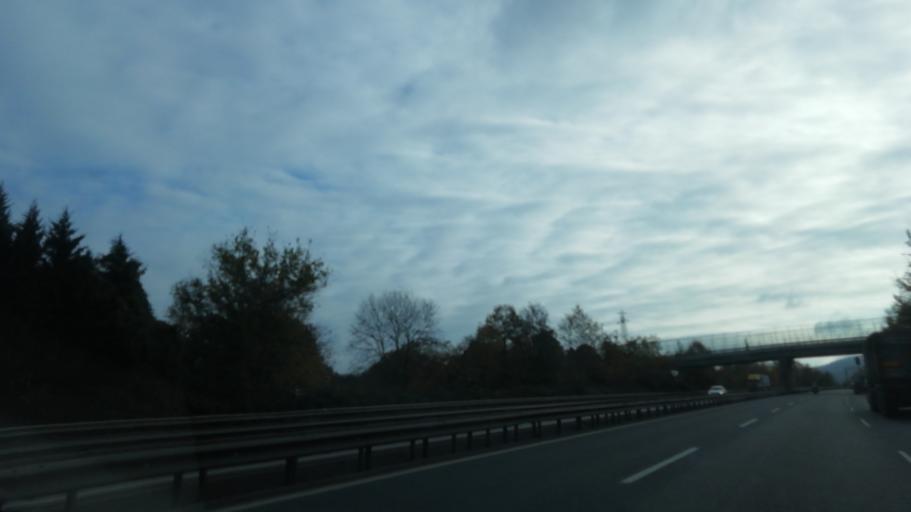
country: TR
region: Sakarya
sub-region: Merkez
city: Sapanca
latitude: 40.6899
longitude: 30.2390
